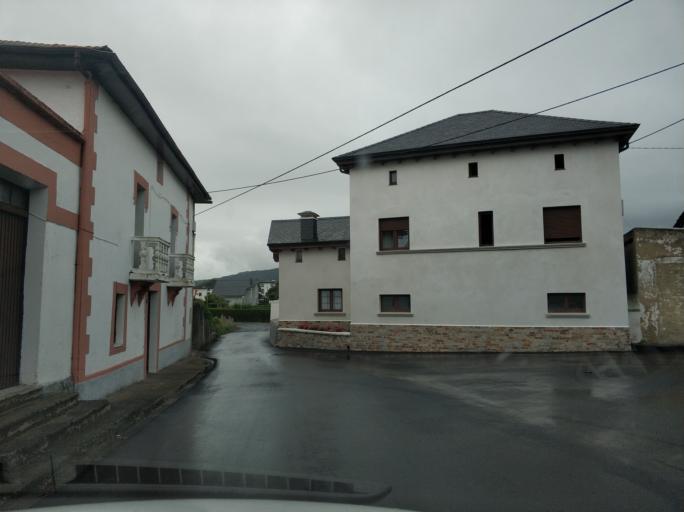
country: ES
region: Asturias
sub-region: Province of Asturias
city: Tineo
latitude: 43.5558
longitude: -6.4634
